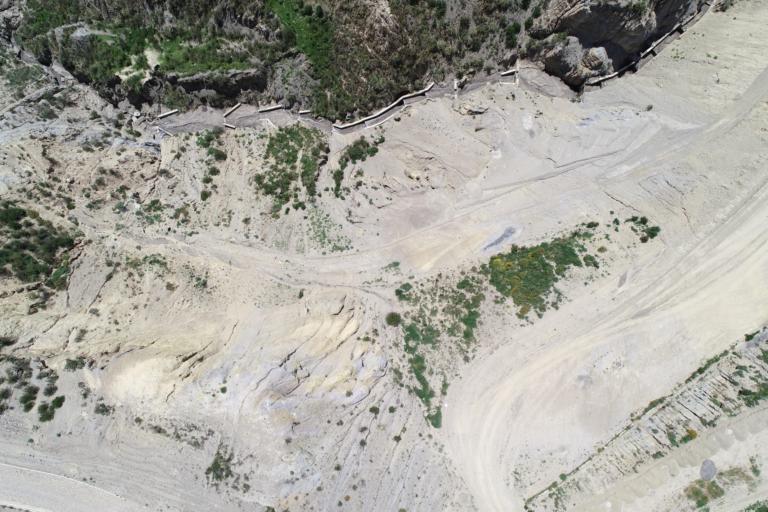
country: BO
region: La Paz
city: La Paz
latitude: -16.5209
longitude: -68.0471
